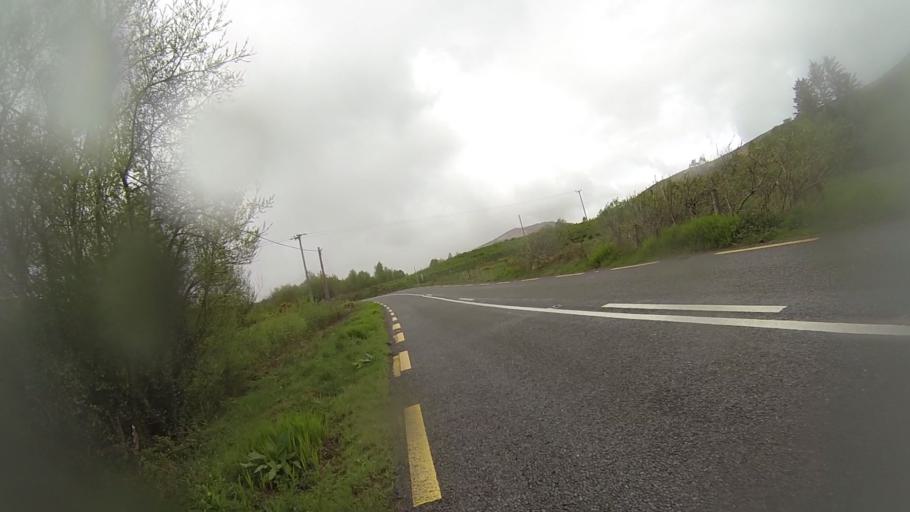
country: IE
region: Munster
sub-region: Ciarrai
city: Kenmare
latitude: 51.8110
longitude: -9.5597
